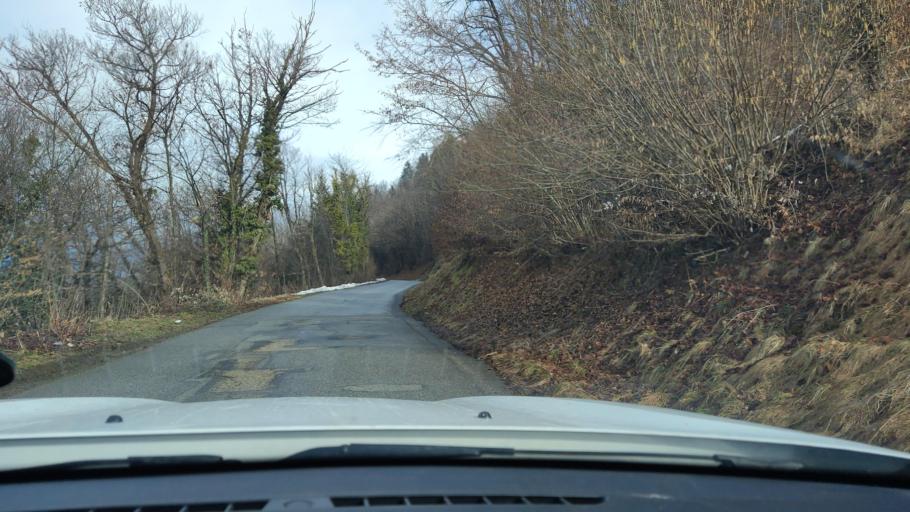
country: FR
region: Rhone-Alpes
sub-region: Departement de la Savoie
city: Marthod
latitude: 45.6967
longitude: 6.4139
